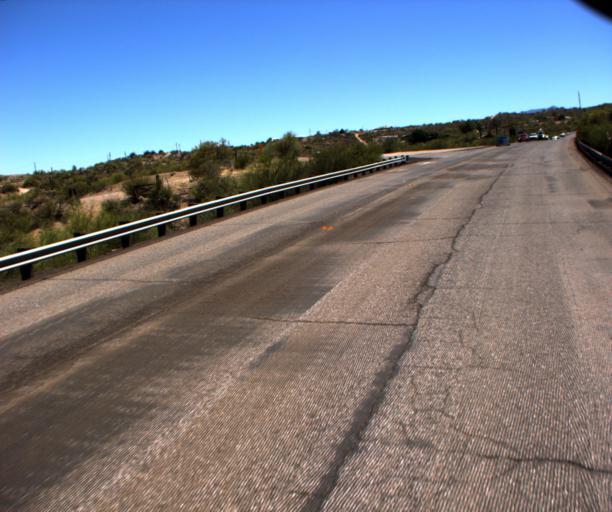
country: US
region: Arizona
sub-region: Pinal County
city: Mammoth
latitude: 32.6958
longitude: -110.6447
